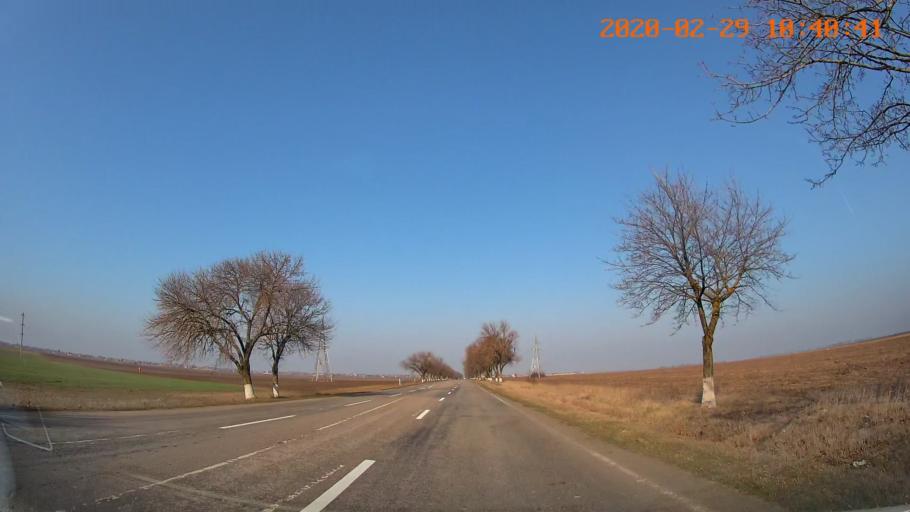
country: MD
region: Anenii Noi
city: Varnita
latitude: 47.0353
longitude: 29.4361
